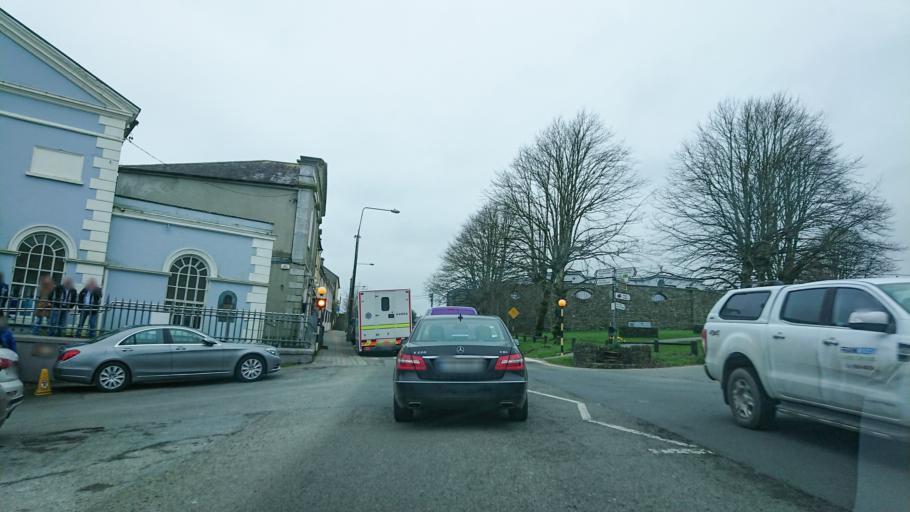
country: IE
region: Munster
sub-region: County Cork
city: Bandon
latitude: 51.7471
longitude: -8.7383
